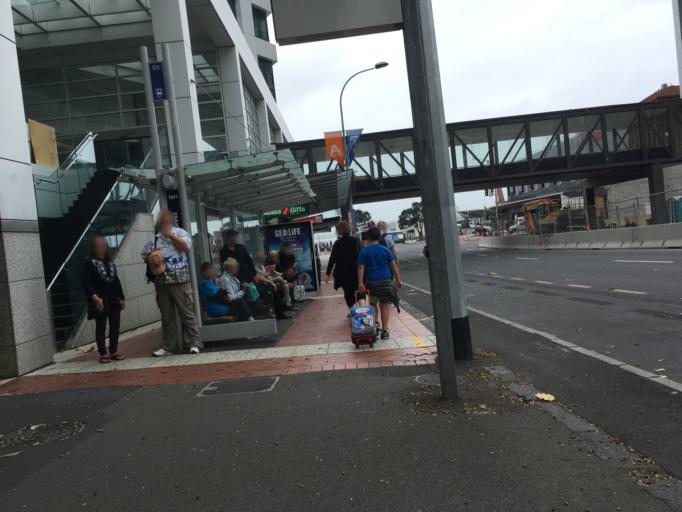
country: NZ
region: Auckland
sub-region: Auckland
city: Auckland
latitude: -36.8440
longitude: 174.7655
